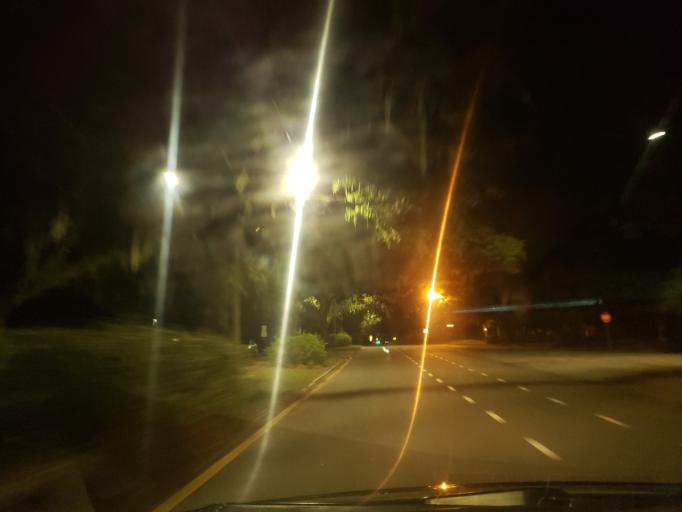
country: US
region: Georgia
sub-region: Chatham County
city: Savannah
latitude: 32.0463
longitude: -81.0906
